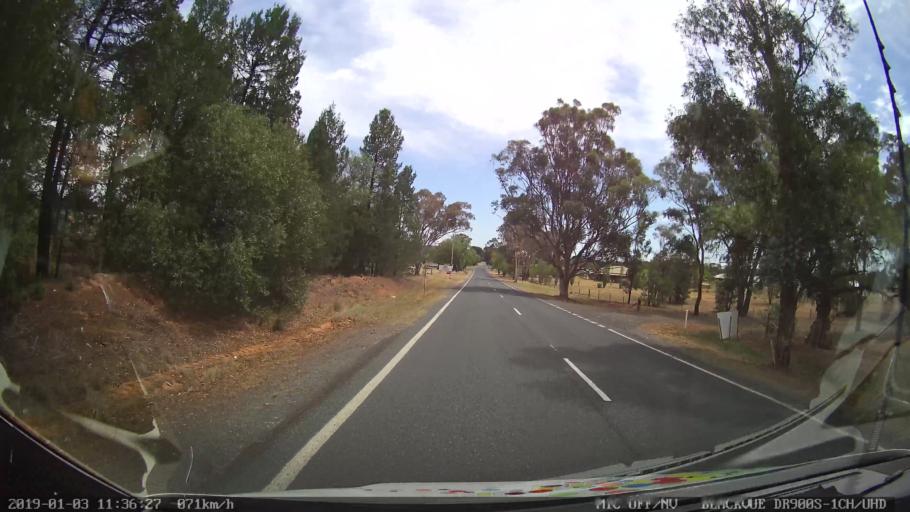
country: AU
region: New South Wales
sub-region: Weddin
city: Grenfell
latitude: -33.9106
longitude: 148.1598
